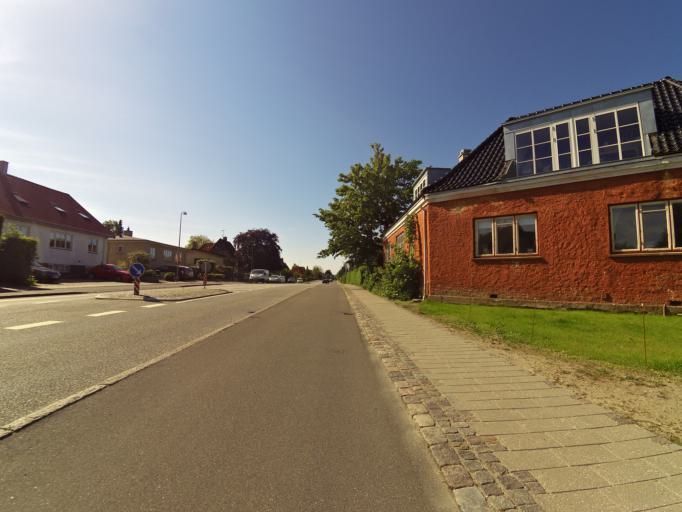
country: DK
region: Capital Region
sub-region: Gladsaxe Municipality
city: Buddinge
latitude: 55.7631
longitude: 12.4940
